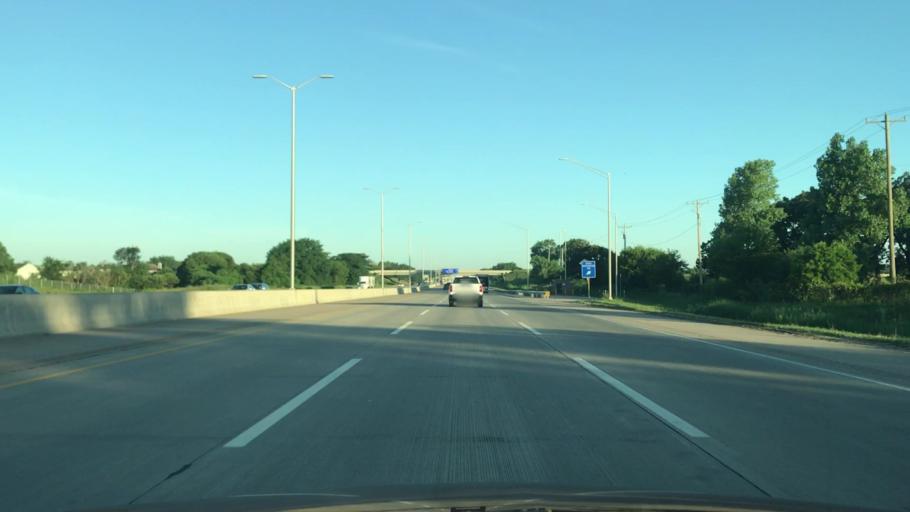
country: US
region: Illinois
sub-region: McHenry County
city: Huntley
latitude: 42.1318
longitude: -88.4628
